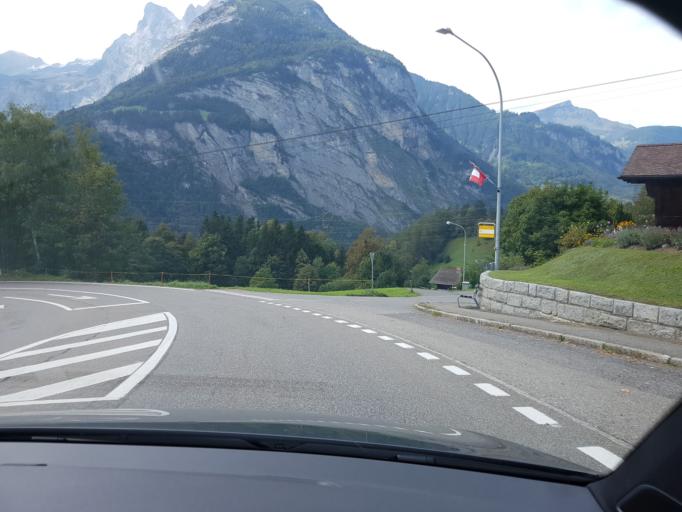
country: CH
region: Bern
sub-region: Interlaken-Oberhasli District
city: Meiringen
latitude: 46.7085
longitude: 8.2355
